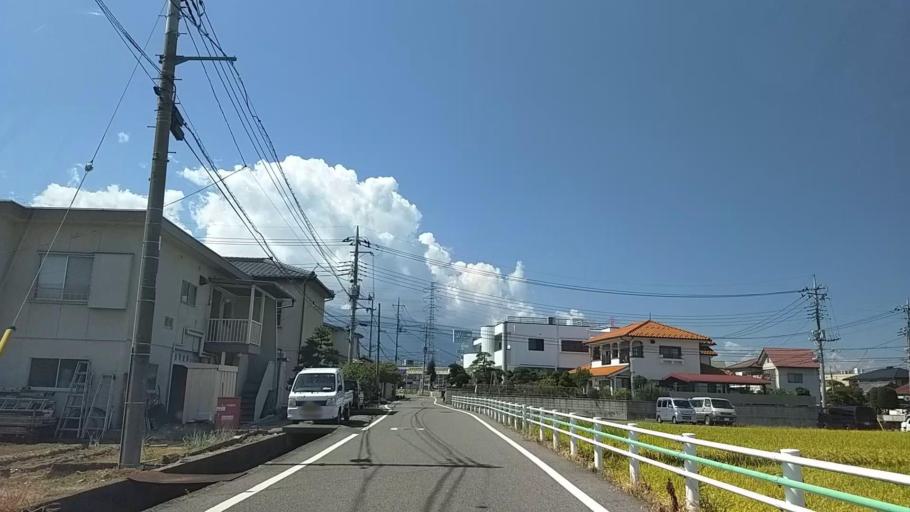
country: JP
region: Yamanashi
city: Ryuo
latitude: 35.6629
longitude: 138.5202
